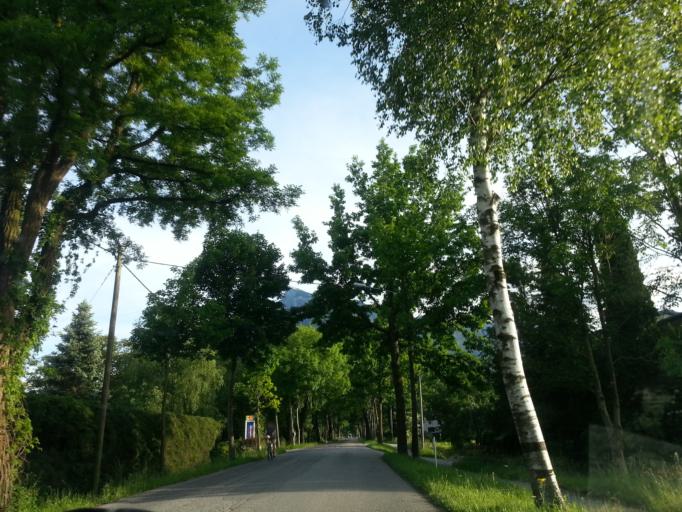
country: AT
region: Salzburg
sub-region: Politischer Bezirk Salzburg-Umgebung
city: Grodig
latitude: 47.7671
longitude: 13.0191
